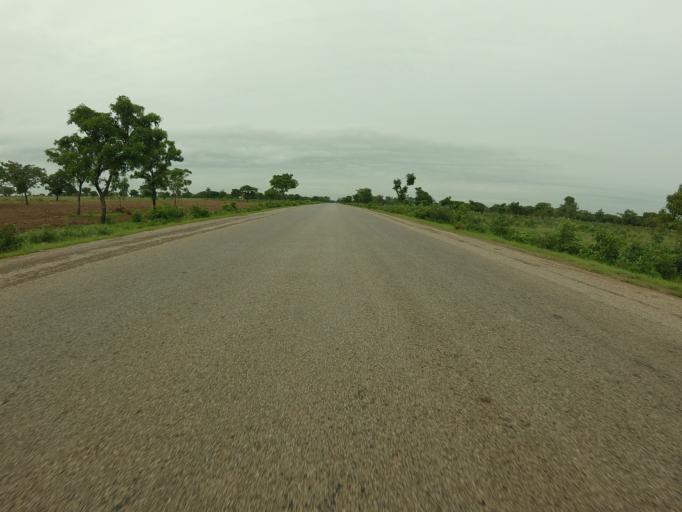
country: GH
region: Northern
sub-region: Yendi
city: Yendi
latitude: 9.5142
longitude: -0.0285
